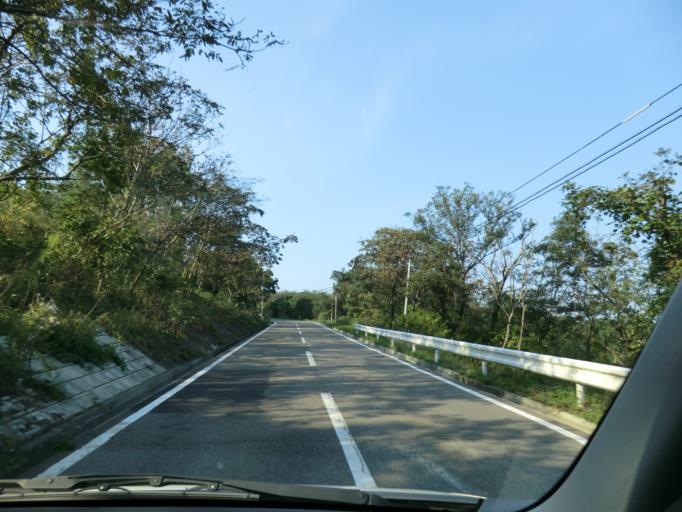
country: JP
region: Niigata
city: Kashiwazaki
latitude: 37.4127
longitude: 138.6094
